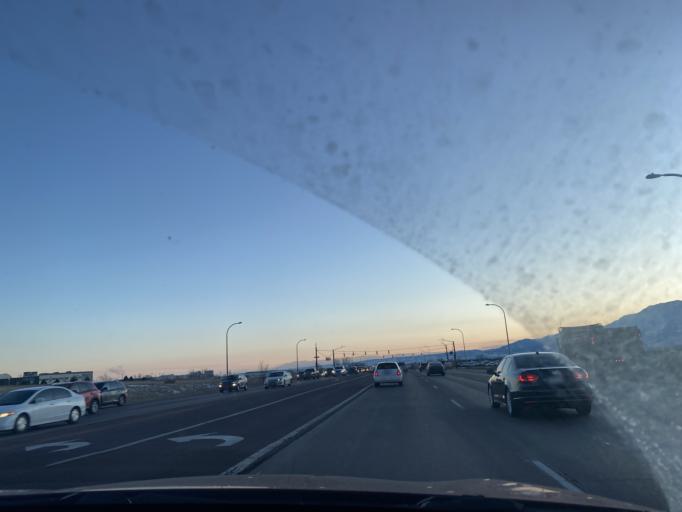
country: US
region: Colorado
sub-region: El Paso County
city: Cimarron Hills
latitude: 38.8265
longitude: -104.7236
